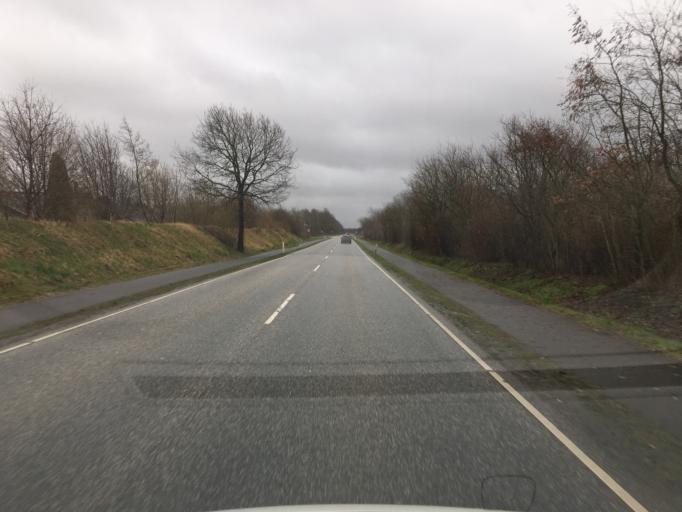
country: DK
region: South Denmark
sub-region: Aabenraa Kommune
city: Tinglev
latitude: 54.9294
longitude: 9.2399
